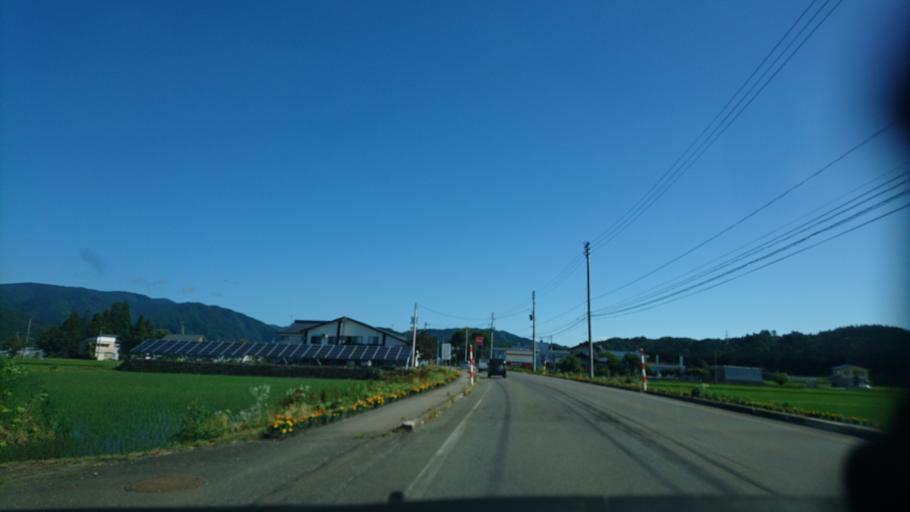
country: JP
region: Akita
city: Kakunodatemachi
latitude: 39.6536
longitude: 140.5709
